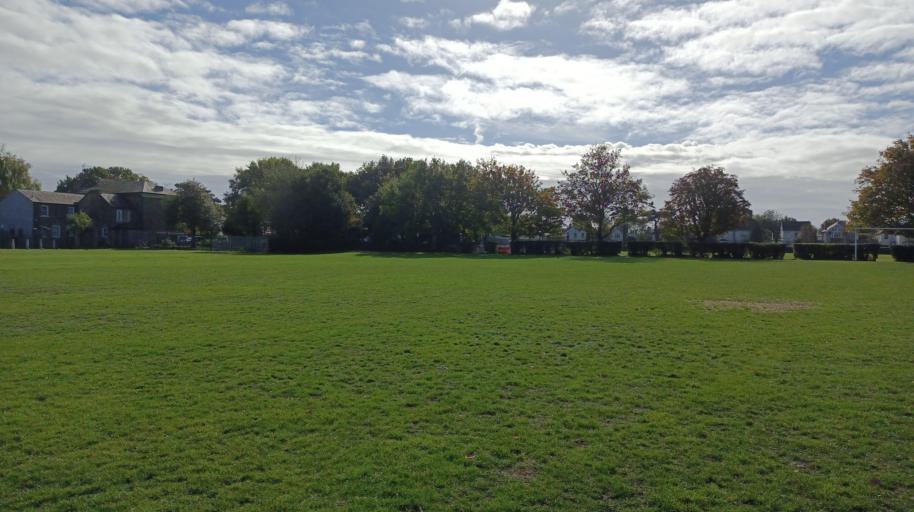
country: GB
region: England
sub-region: Essex
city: Hadleigh
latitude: 51.5578
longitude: 0.6091
